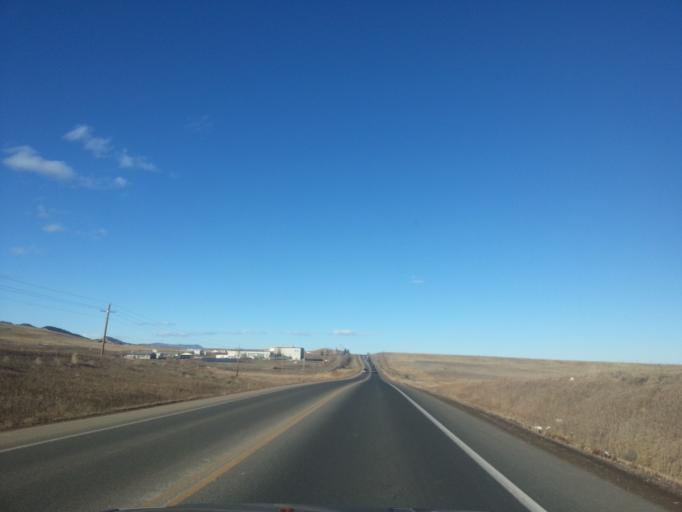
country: US
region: Colorado
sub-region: Larimer County
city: Fort Collins
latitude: 40.4986
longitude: -105.1154
